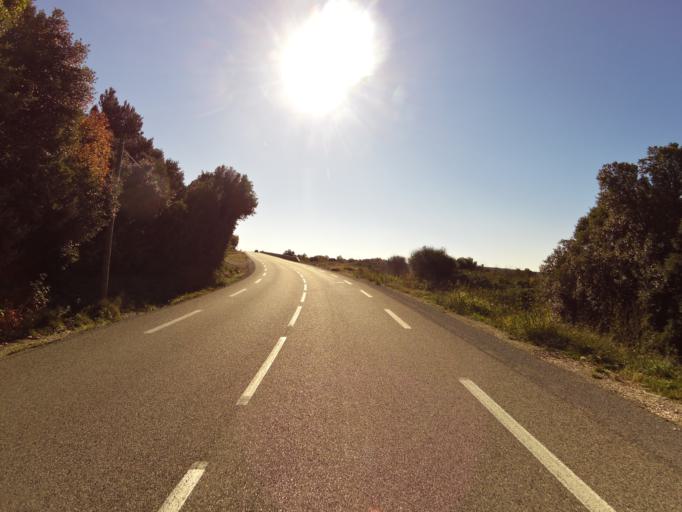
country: FR
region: Languedoc-Roussillon
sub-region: Departement du Gard
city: Saint-Julien-de-Peyrolas
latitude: 44.4002
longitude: 4.4803
